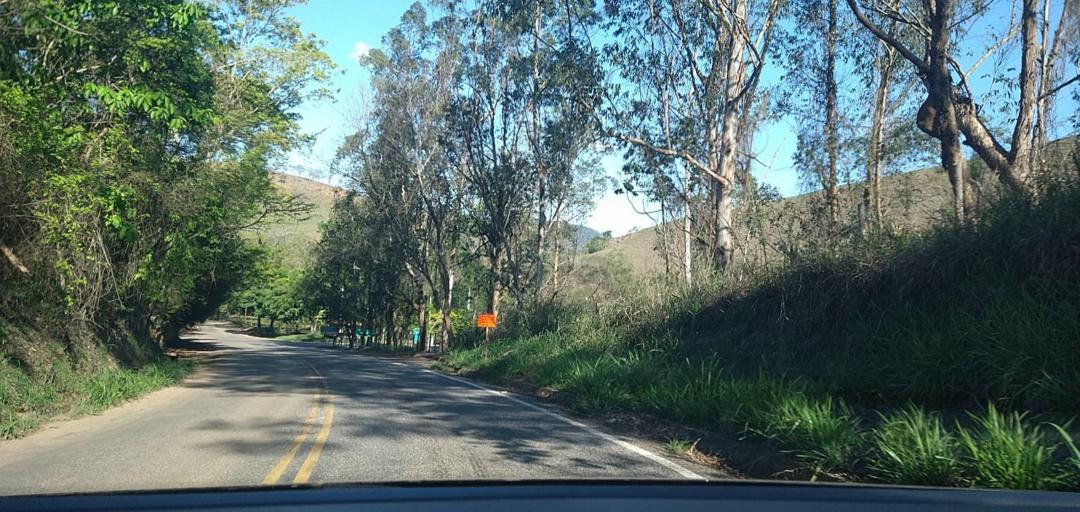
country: BR
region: Minas Gerais
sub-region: Ponte Nova
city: Ponte Nova
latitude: -20.2467
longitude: -42.8920
